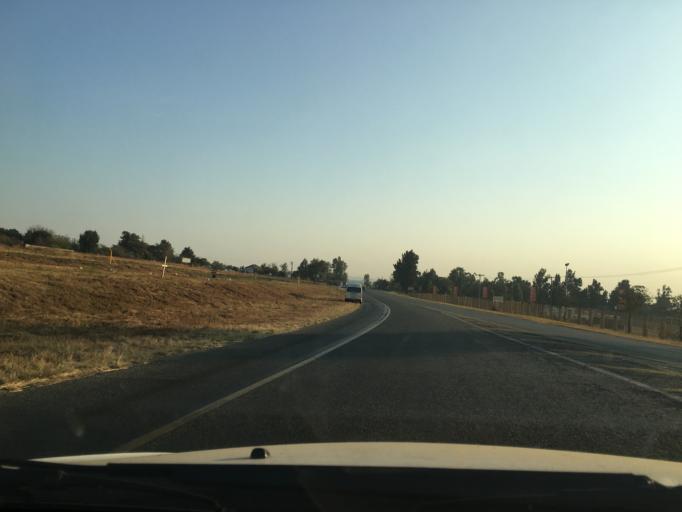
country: ZA
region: Gauteng
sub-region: West Rand District Municipality
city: Muldersdriseloop
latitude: -26.0163
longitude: 27.8590
